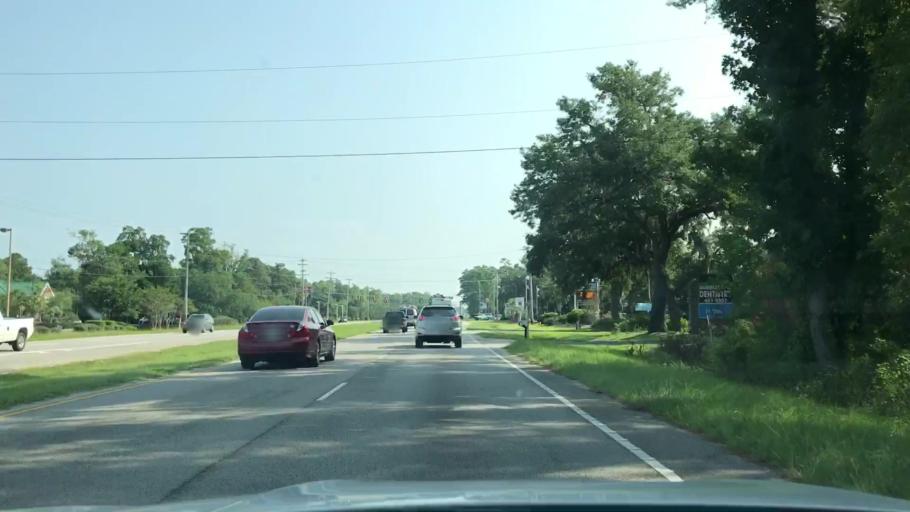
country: US
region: South Carolina
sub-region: Georgetown County
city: Murrells Inlet
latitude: 33.5539
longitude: -79.0454
